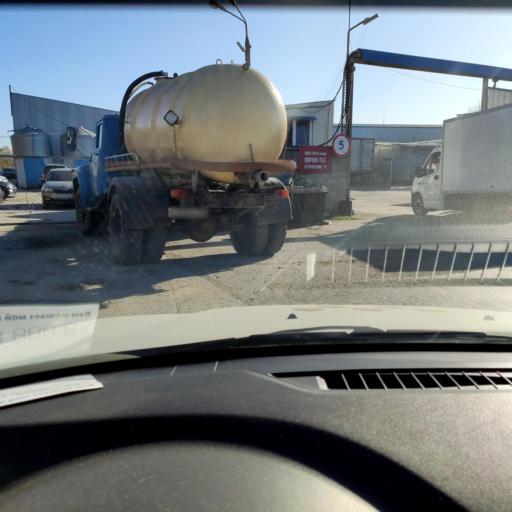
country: RU
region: Samara
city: Tol'yatti
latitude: 53.5308
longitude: 49.4539
